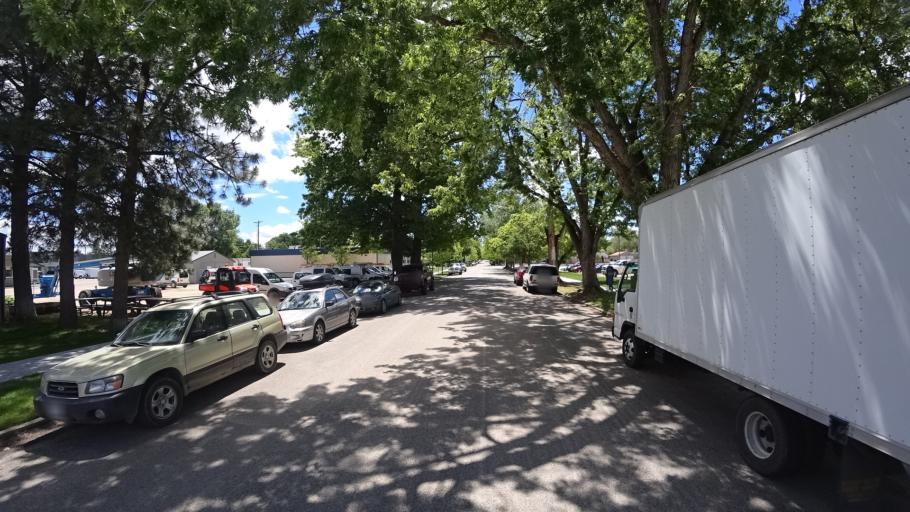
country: US
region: Idaho
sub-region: Ada County
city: Boise
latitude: 43.5997
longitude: -116.1986
